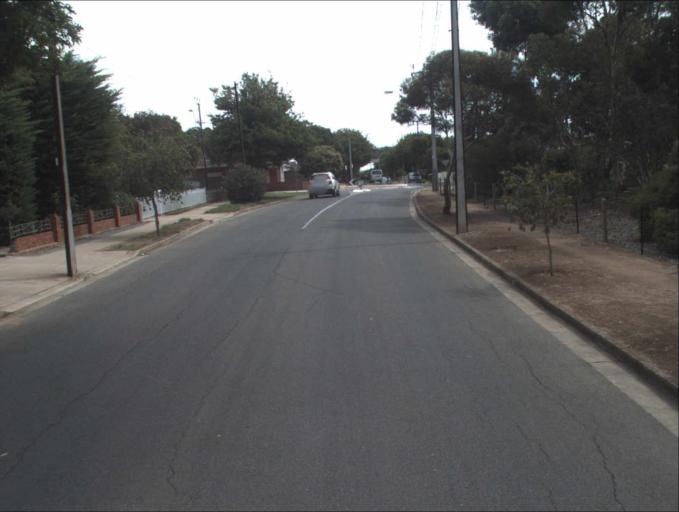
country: AU
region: South Australia
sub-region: Port Adelaide Enfield
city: Enfield
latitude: -34.8604
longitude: 138.6089
